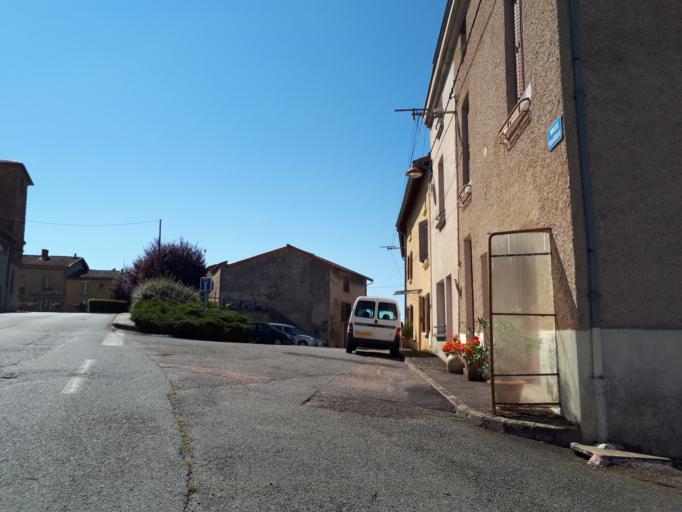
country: FR
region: Rhone-Alpes
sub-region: Departement de la Loire
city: Bussieres
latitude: 45.8374
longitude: 4.2658
